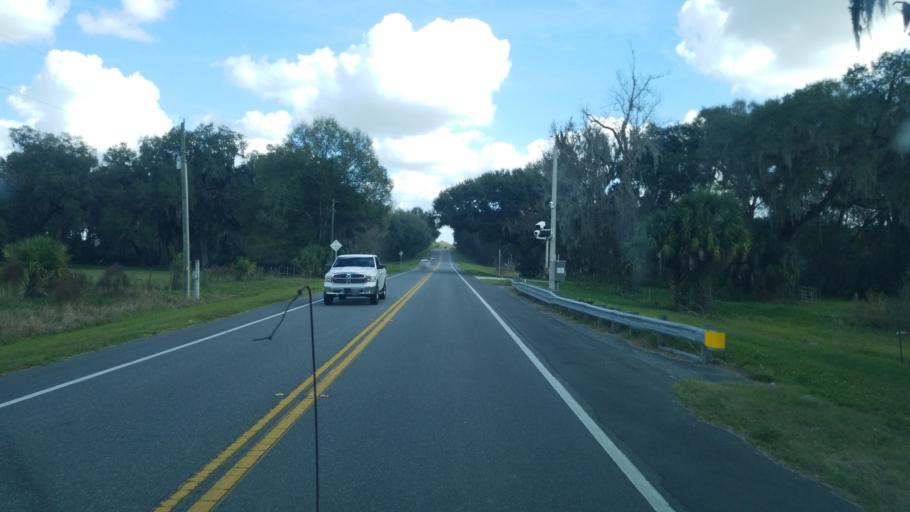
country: US
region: Florida
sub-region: Sumter County
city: Wildwood
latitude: 28.9308
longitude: -82.1175
